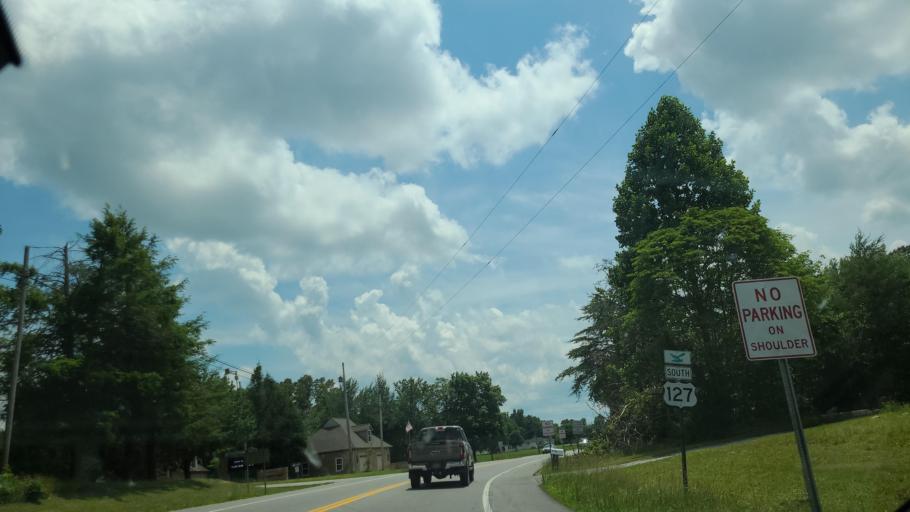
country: US
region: Tennessee
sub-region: Cumberland County
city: Crossville
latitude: 35.9040
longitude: -84.9857
